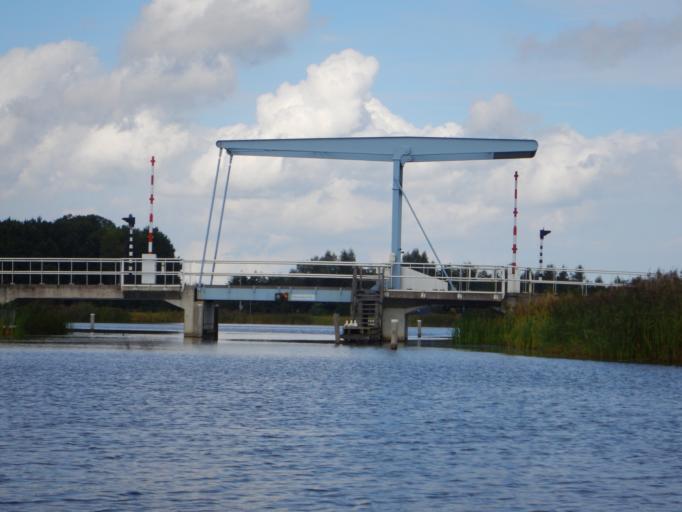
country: NL
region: Groningen
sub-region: Gemeente  Oldambt
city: Winschoten
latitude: 53.1747
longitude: 7.0495
